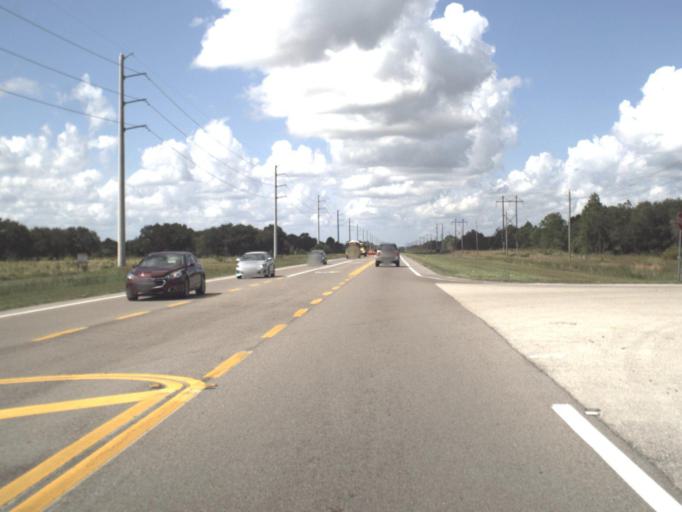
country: US
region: Florida
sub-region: Lee County
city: Gateway
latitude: 26.5679
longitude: -81.6818
